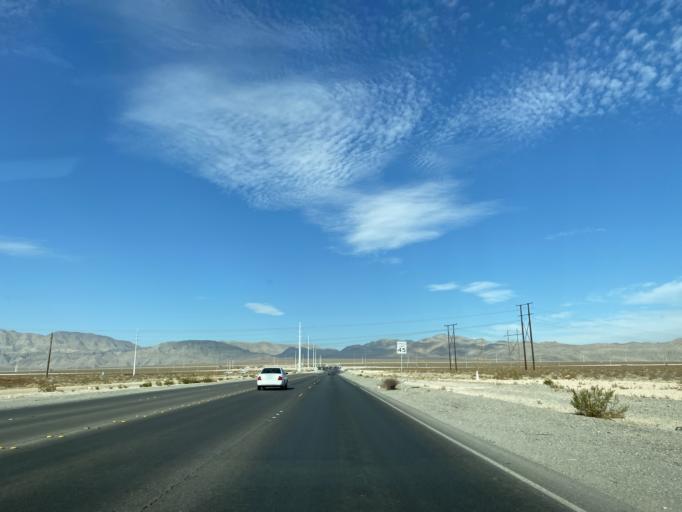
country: US
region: Nevada
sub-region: Clark County
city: Nellis Air Force Base
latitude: 36.2798
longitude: -115.0799
